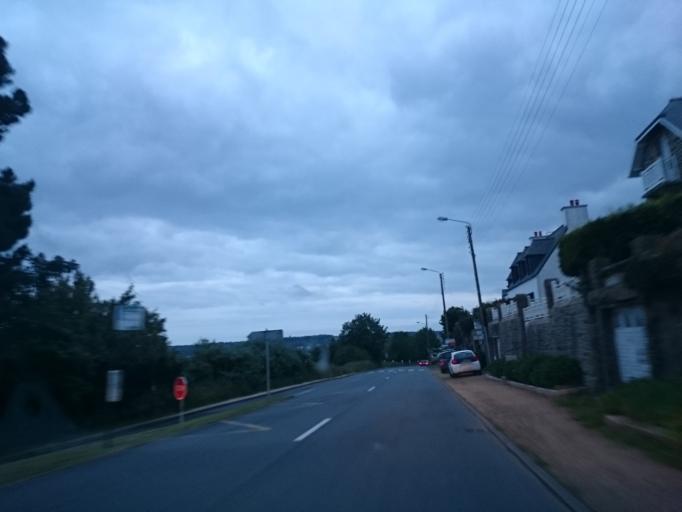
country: FR
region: Brittany
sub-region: Departement des Cotes-d'Armor
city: Perros-Guirec
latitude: 48.8142
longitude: -3.4345
